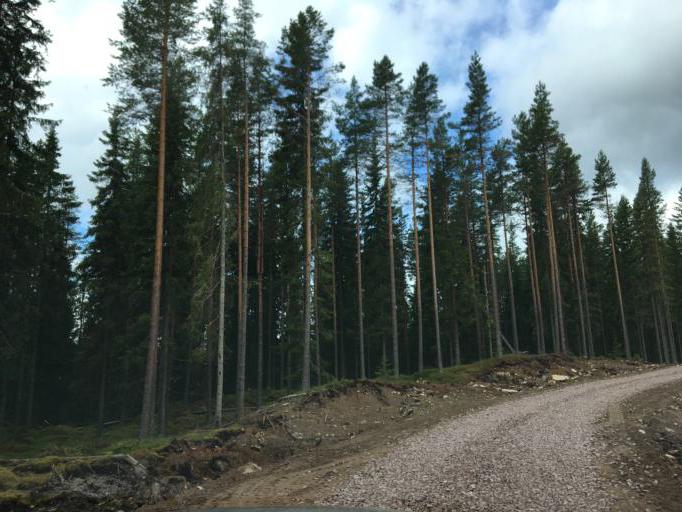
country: SE
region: Vaermland
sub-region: Filipstads Kommun
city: Lesjofors
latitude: 60.0825
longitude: 14.4694
